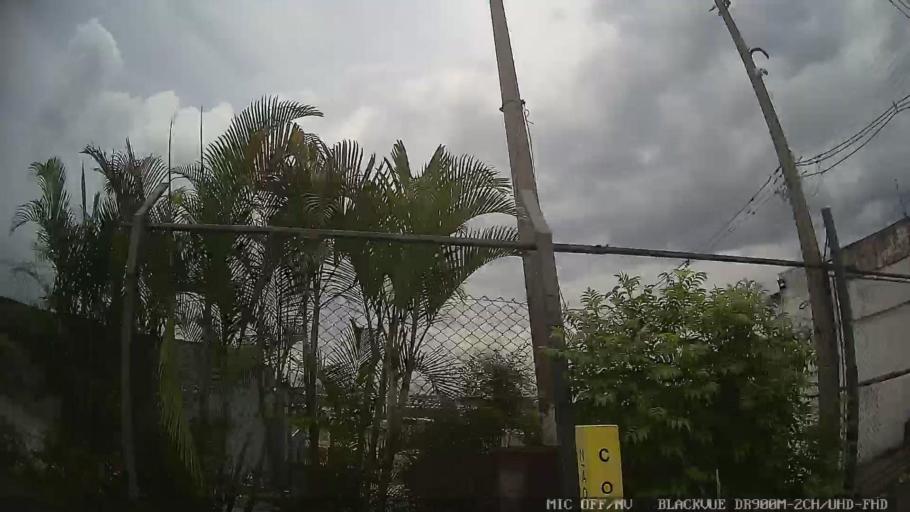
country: BR
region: Sao Paulo
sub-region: Aruja
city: Aruja
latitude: -23.4439
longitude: -46.3185
